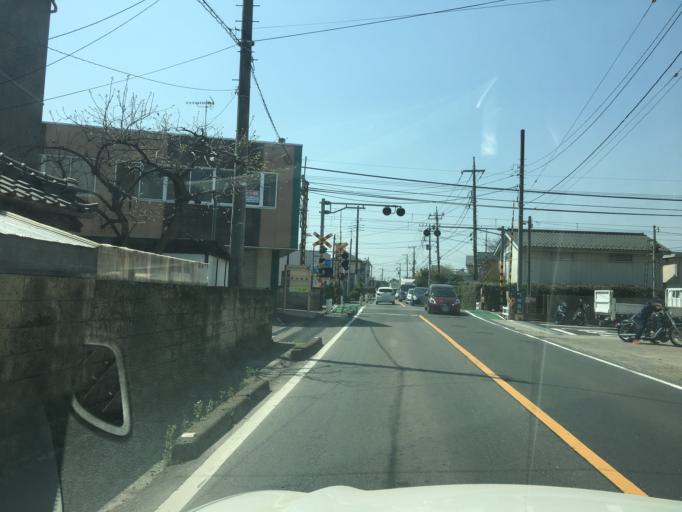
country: JP
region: Saitama
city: Sayama
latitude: 35.8341
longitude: 139.4260
